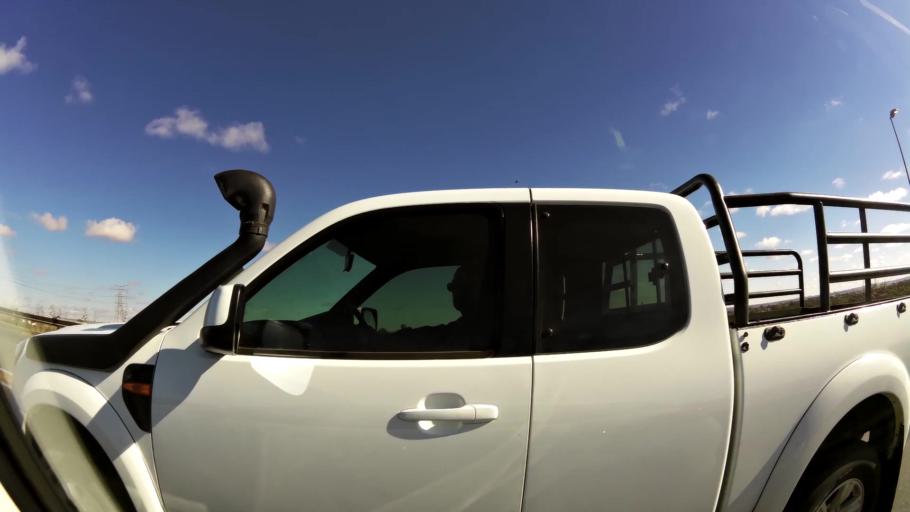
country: ZA
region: Limpopo
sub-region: Capricorn District Municipality
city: Polokwane
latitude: -23.8780
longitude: 29.4610
